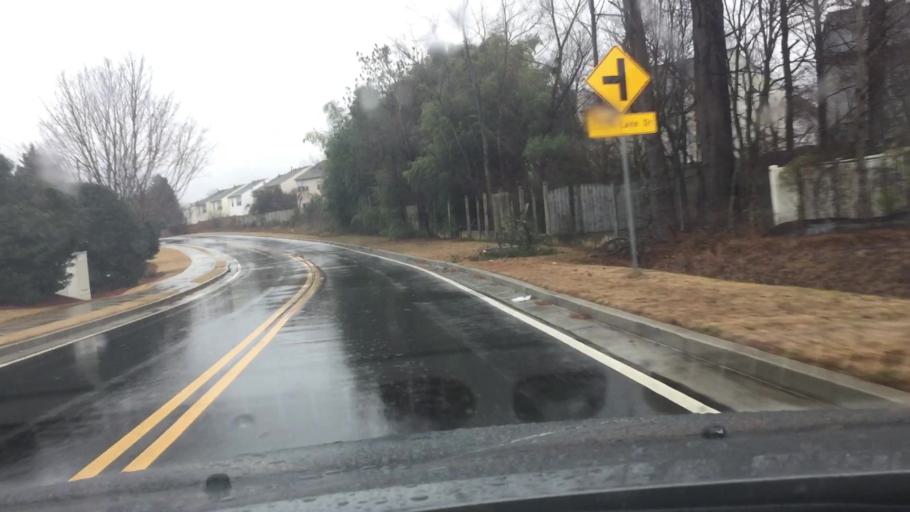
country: US
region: Georgia
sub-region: Cobb County
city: Kennesaw
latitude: 33.9946
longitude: -84.6026
